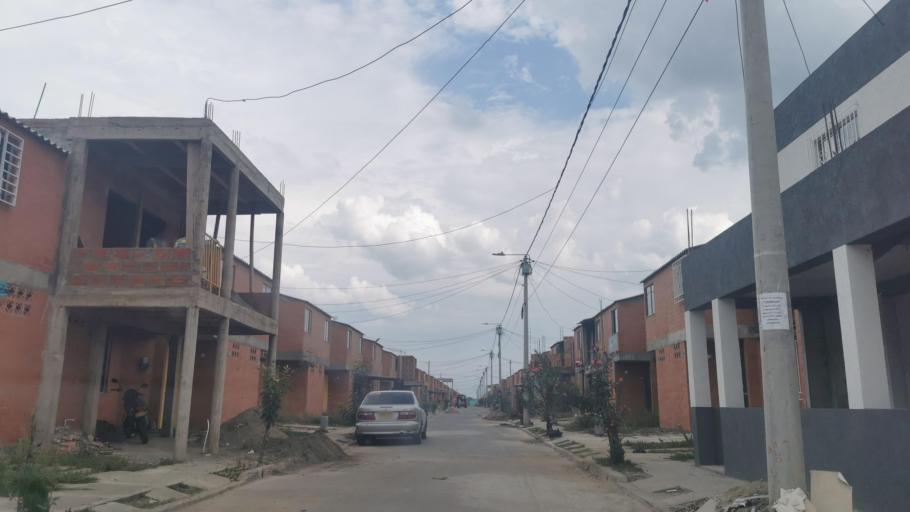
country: CO
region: Valle del Cauca
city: Jamundi
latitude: 3.2354
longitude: -76.5253
